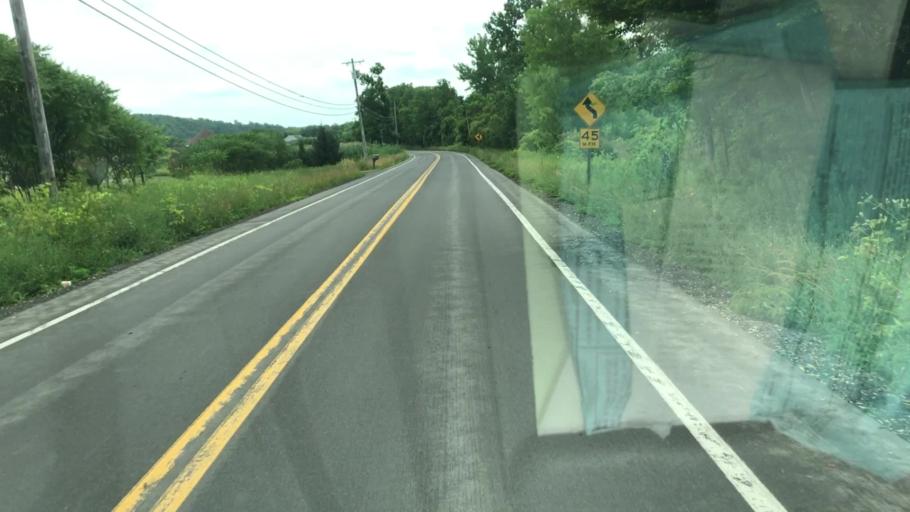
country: US
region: New York
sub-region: Onondaga County
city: Manlius
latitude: 42.9721
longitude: -75.9886
